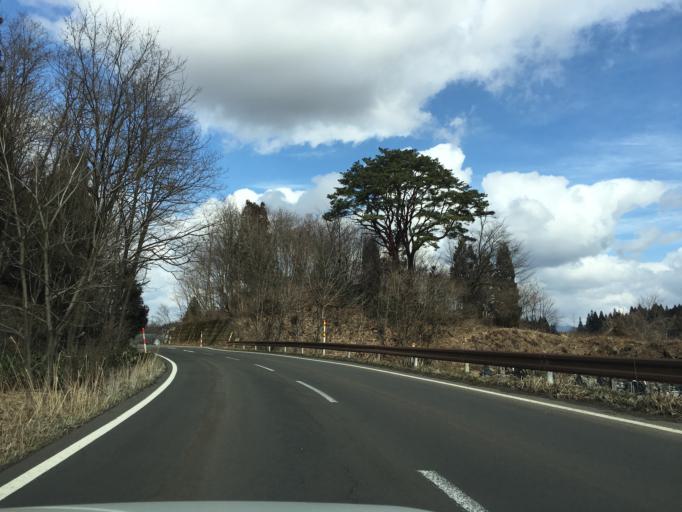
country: JP
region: Akita
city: Odate
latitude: 40.1962
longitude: 140.5346
